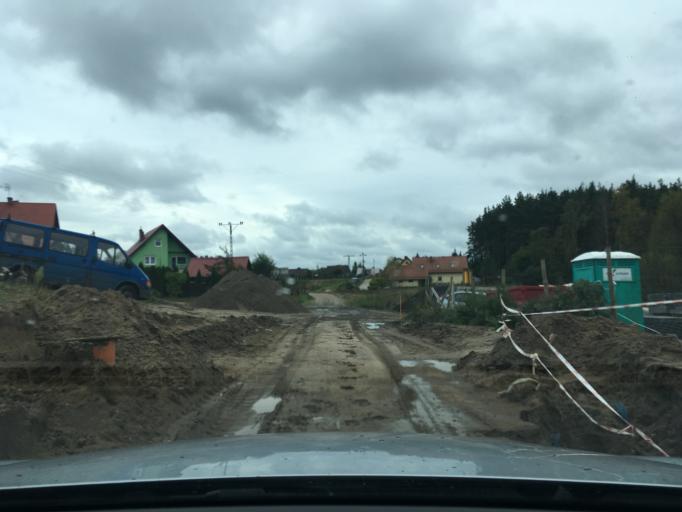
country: PL
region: Pomeranian Voivodeship
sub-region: Powiat koscierski
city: Koscierzyna
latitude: 54.1026
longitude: 17.9715
